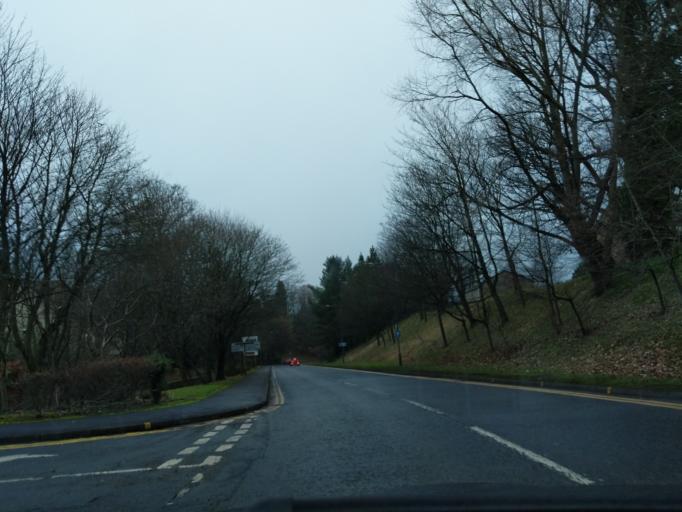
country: GB
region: Scotland
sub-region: Falkirk
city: Falkirk
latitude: 55.9995
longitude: -3.7893
